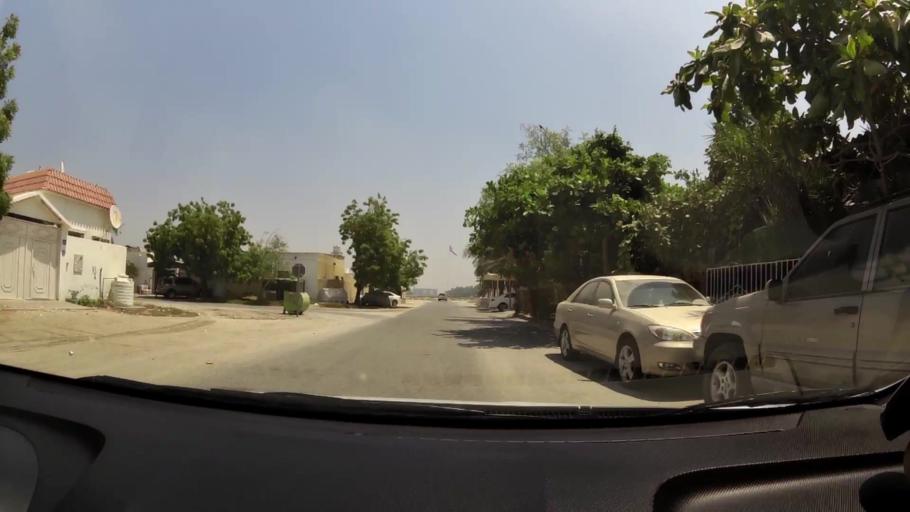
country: AE
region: Umm al Qaywayn
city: Umm al Qaywayn
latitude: 25.5606
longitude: 55.5610
